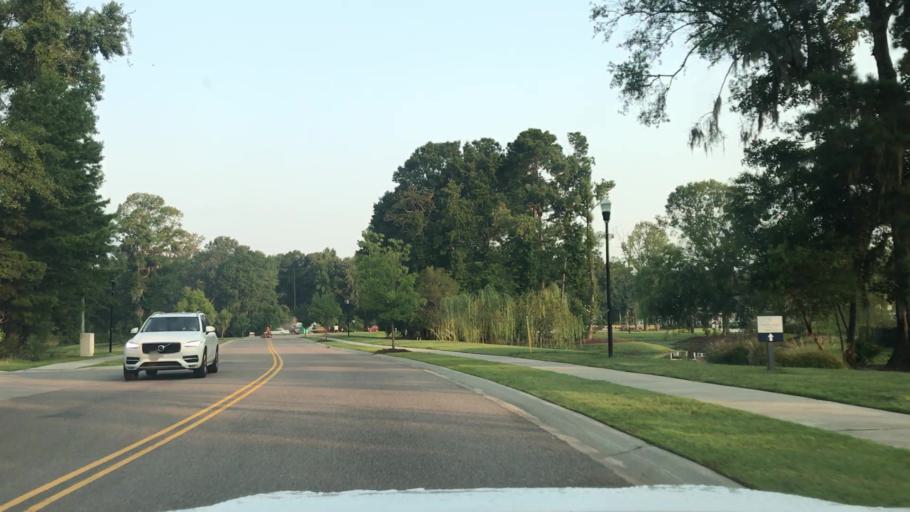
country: US
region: South Carolina
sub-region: Charleston County
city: Shell Point
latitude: 32.8260
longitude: -80.0963
